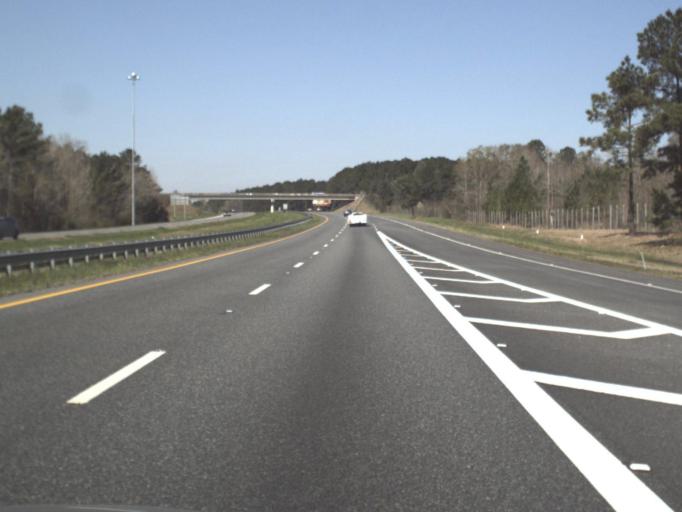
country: US
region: Florida
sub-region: Jackson County
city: Marianna
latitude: 30.7552
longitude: -85.2766
